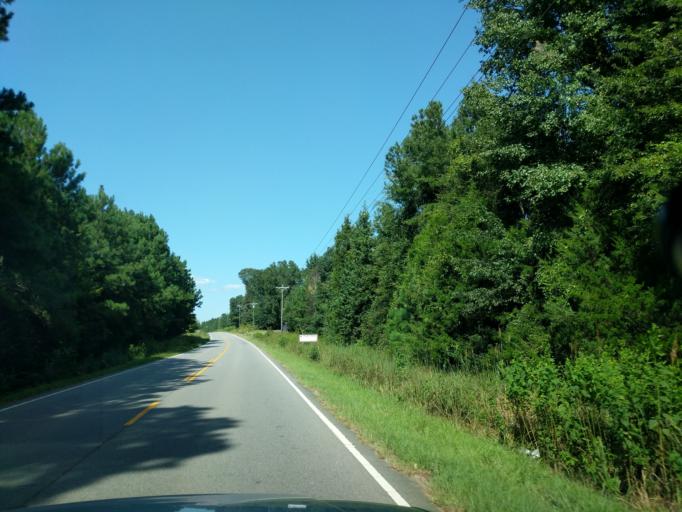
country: US
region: South Carolina
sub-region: Newberry County
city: Prosperity
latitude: 34.1464
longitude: -81.5321
